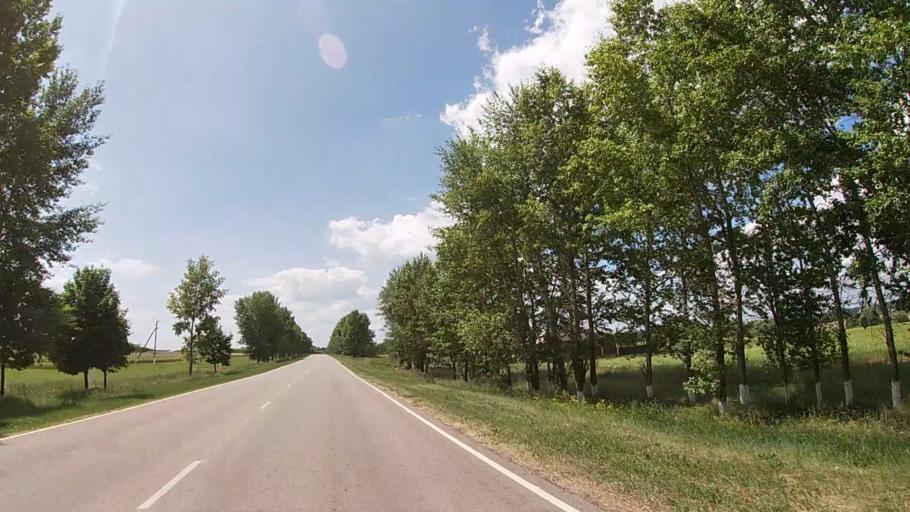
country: RU
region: Belgorod
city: Grayvoron
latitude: 50.4398
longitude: 35.6114
